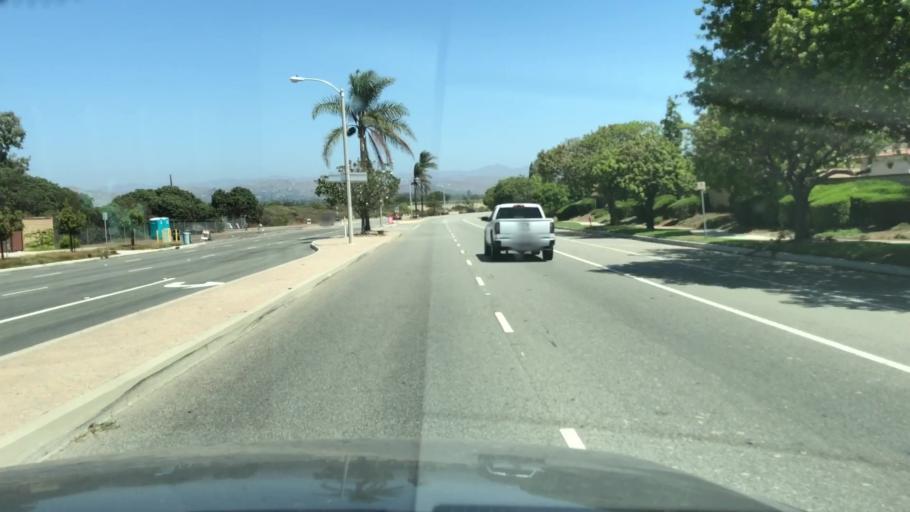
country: US
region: California
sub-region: Ventura County
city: El Rio
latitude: 34.2328
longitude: -119.1944
